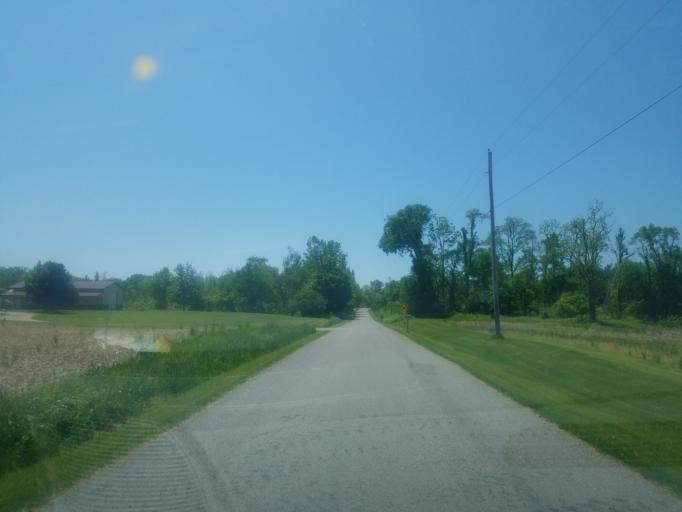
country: US
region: Ohio
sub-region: Huron County
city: Wakeman
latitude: 41.1889
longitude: -82.3701
